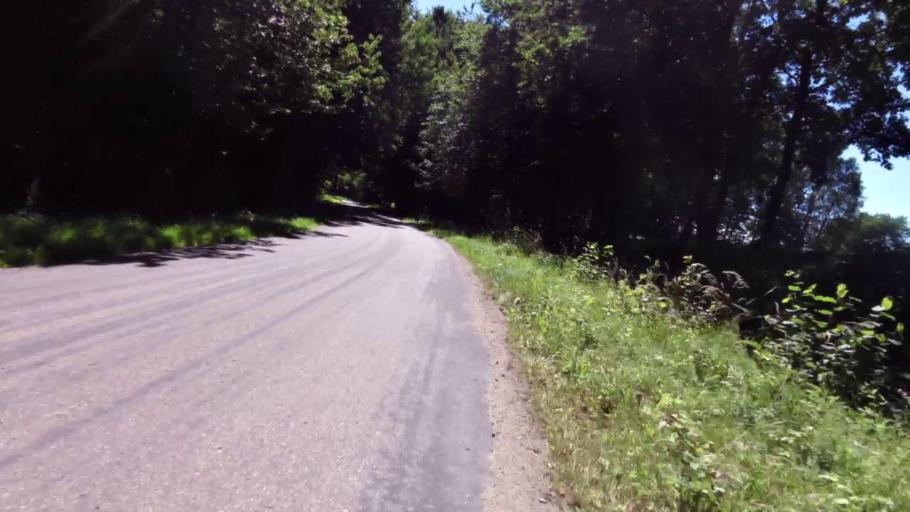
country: PL
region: West Pomeranian Voivodeship
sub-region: Powiat szczecinecki
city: Bialy Bor
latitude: 53.9690
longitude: 16.8641
